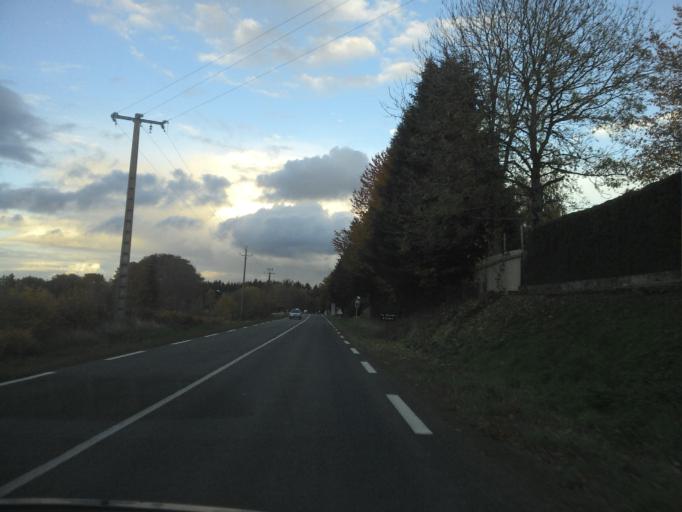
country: FR
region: Auvergne
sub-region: Departement du Puy-de-Dome
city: Chapdes-Beaufort
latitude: 45.8420
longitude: 2.8048
